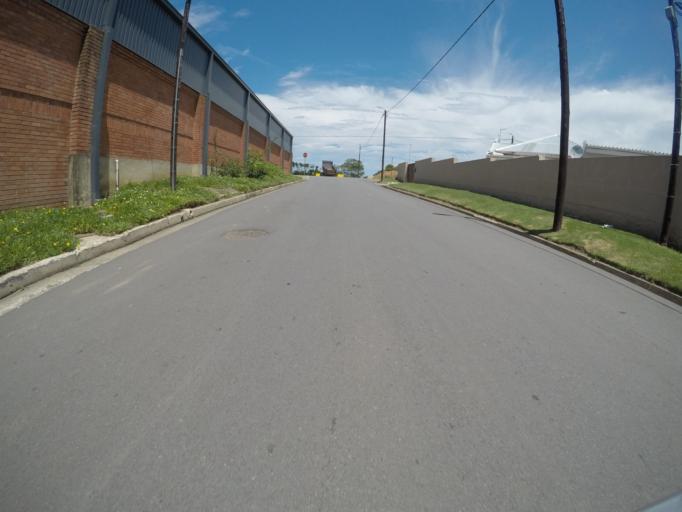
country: ZA
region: Eastern Cape
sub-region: Buffalo City Metropolitan Municipality
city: East London
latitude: -33.0350
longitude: 27.8540
